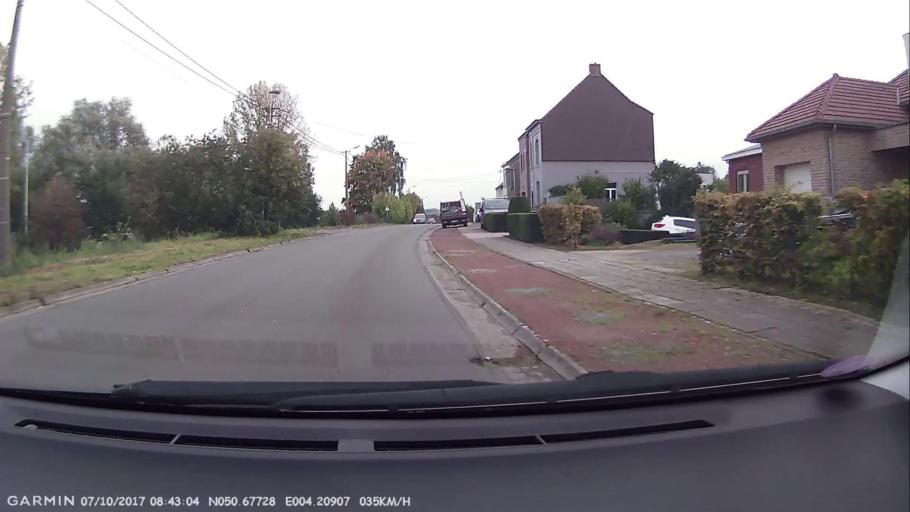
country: BE
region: Wallonia
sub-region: Province du Brabant Wallon
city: Tubize
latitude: 50.6774
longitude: 4.2091
